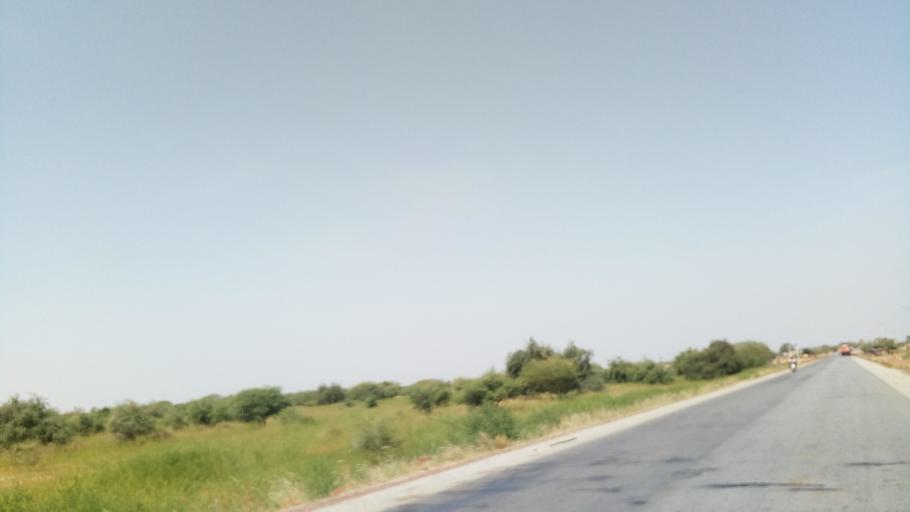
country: ML
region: Kayes
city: Kayes
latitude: 14.3944
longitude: -11.4616
